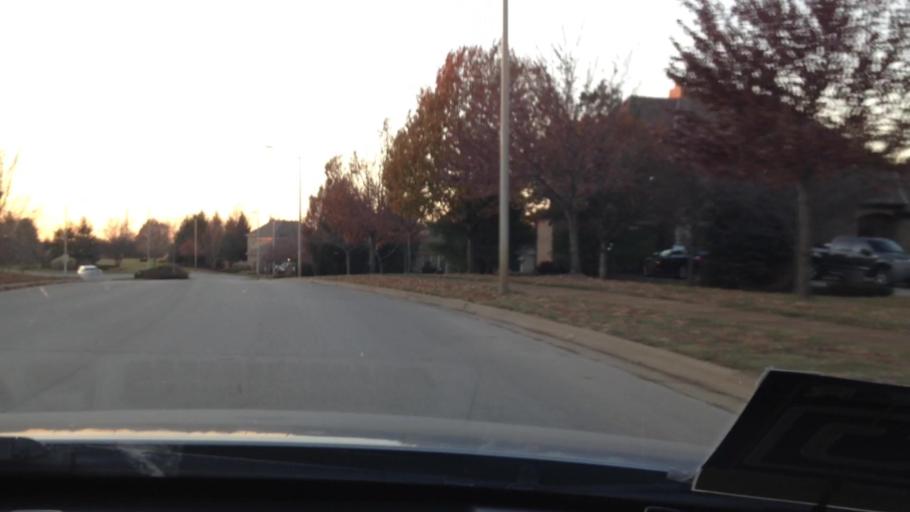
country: US
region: Missouri
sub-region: Clay County
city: Gladstone
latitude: 39.2843
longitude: -94.5544
